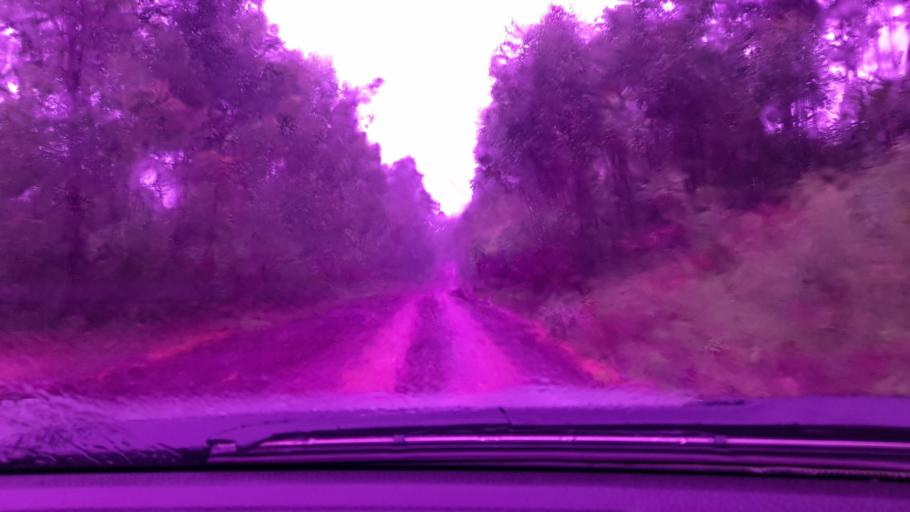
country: ET
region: Oromiya
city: Metu
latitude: 8.3550
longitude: 35.5974
